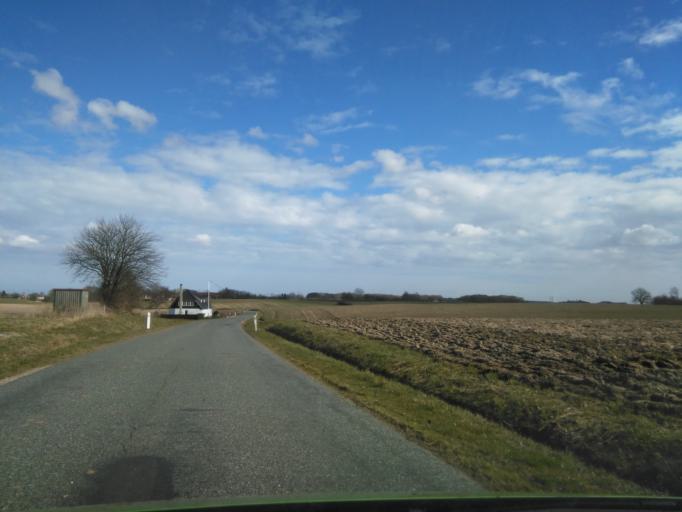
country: DK
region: Central Jutland
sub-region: Skanderborg Kommune
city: Skanderborg
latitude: 55.9184
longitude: 9.9811
